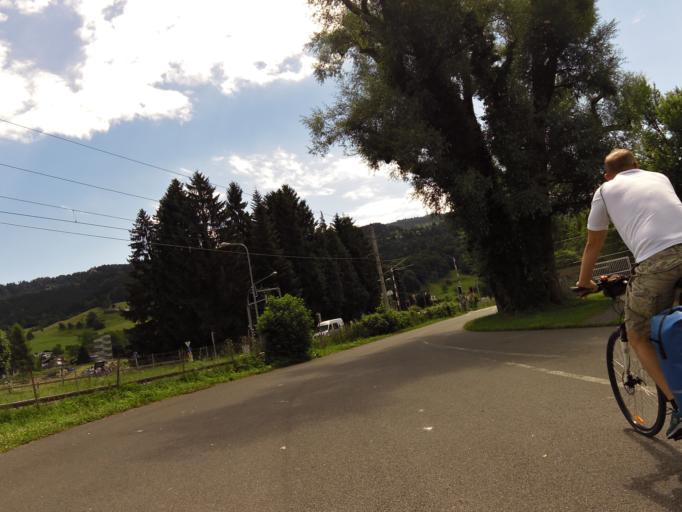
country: AT
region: Vorarlberg
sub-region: Politischer Bezirk Bregenz
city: Lochau
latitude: 47.5263
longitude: 9.7460
